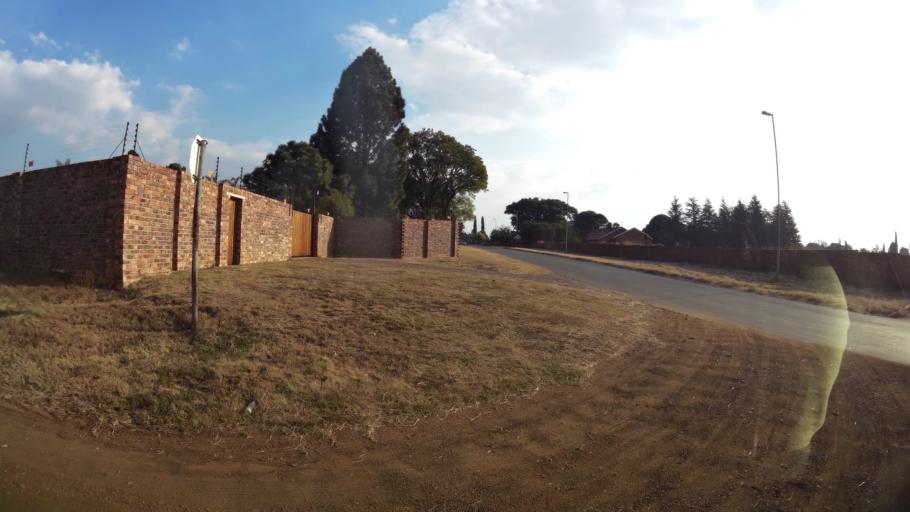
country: ZA
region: Gauteng
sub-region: Ekurhuleni Metropolitan Municipality
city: Benoni
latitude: -26.1063
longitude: 28.2842
